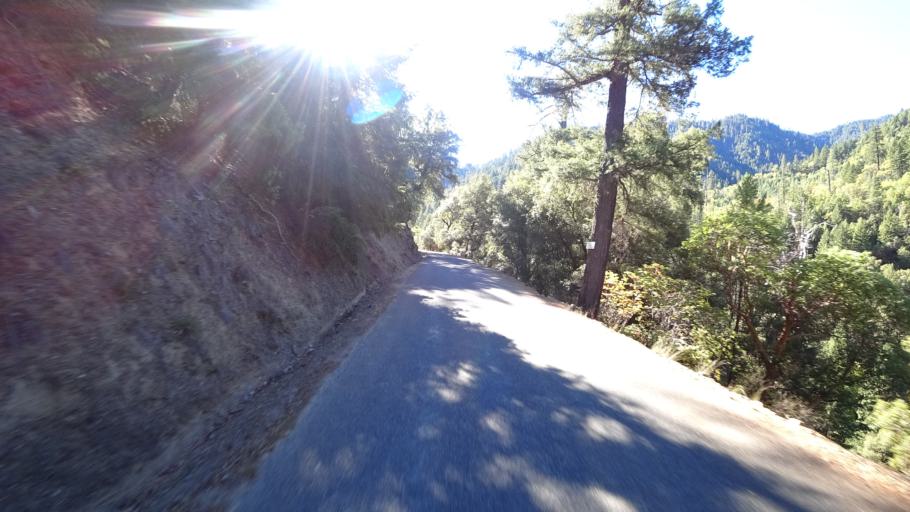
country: US
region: California
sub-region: Humboldt County
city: Willow Creek
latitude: 41.1704
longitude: -123.2189
